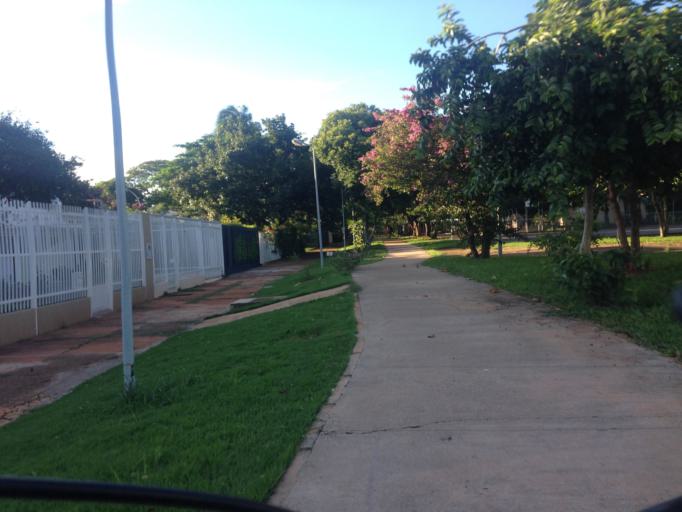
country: BR
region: Federal District
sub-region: Brasilia
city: Brasilia
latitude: -15.8112
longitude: -47.9064
